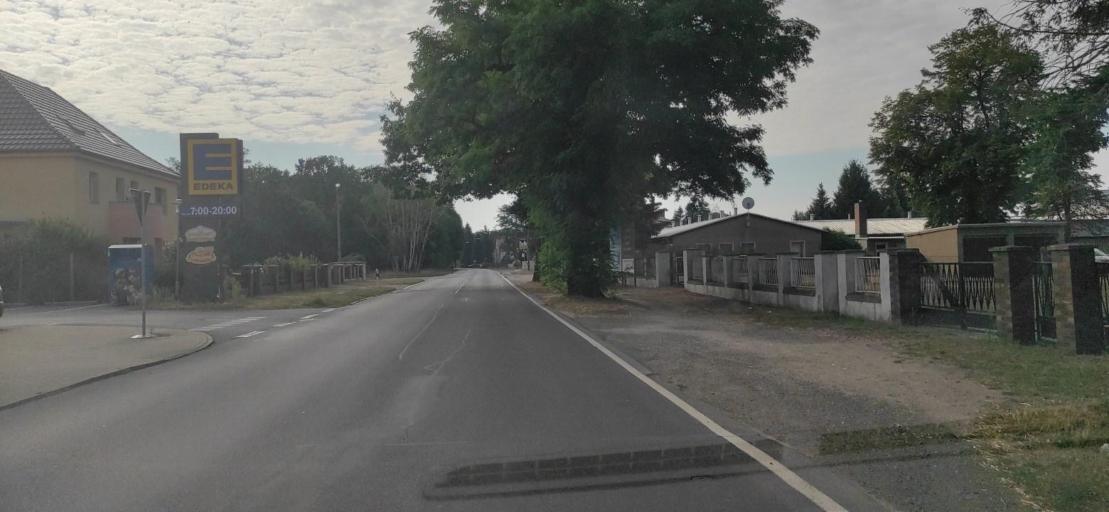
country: DE
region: Brandenburg
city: Forst
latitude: 51.7274
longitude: 14.6473
